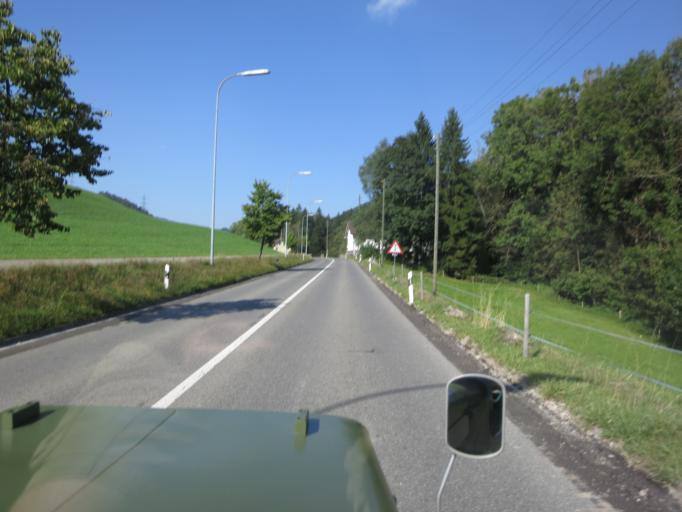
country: CH
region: Zurich
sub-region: Bezirk Hinwil
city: Wald
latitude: 47.2883
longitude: 8.9165
